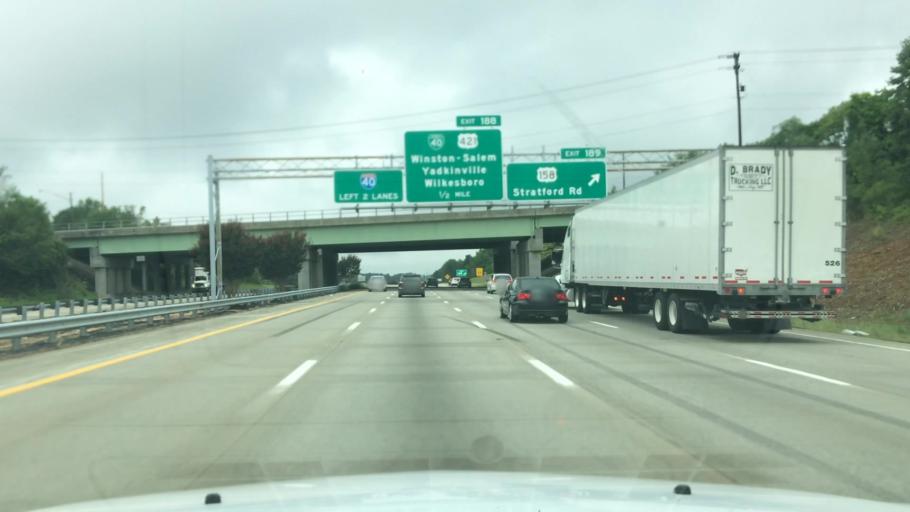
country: US
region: North Carolina
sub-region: Forsyth County
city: Winston-Salem
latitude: 36.0659
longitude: -80.3065
